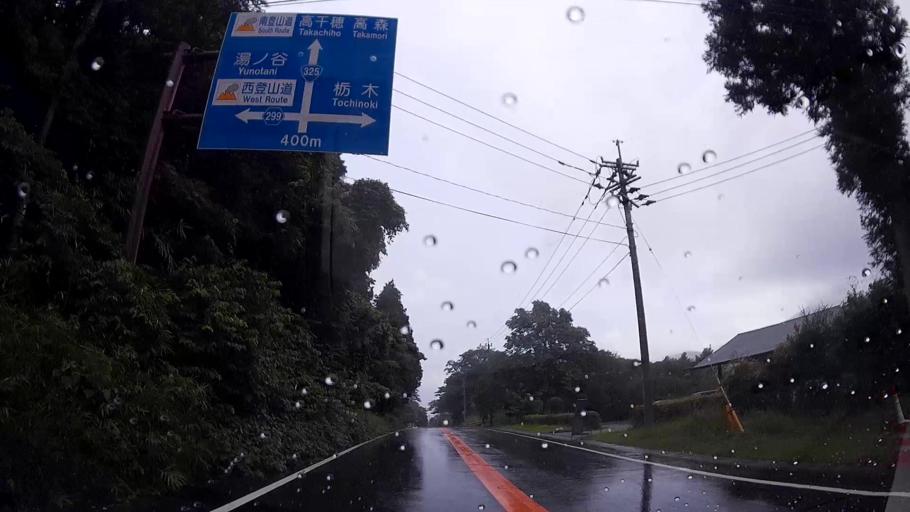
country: JP
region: Kumamoto
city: Aso
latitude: 32.8745
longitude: 130.9920
